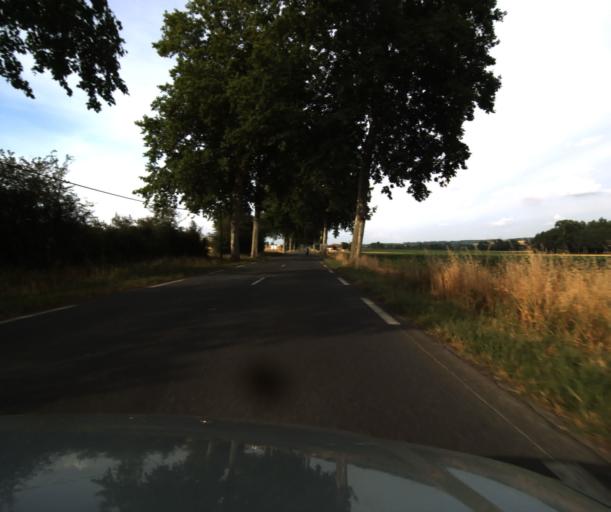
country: FR
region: Midi-Pyrenees
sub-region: Departement du Tarn-et-Garonne
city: Beaumont-de-Lomagne
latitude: 43.9054
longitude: 1.0387
